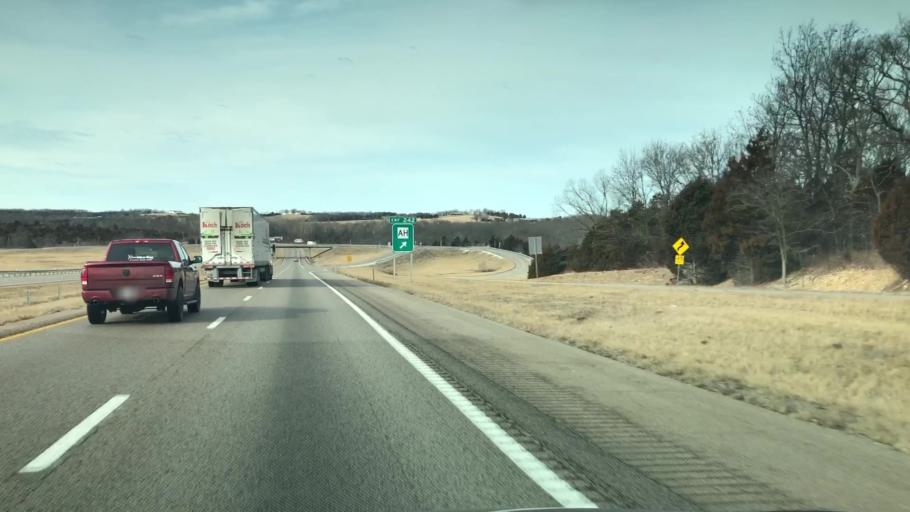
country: US
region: Missouri
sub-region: Franklin County
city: Saint Clair
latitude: 38.3850
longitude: -90.9559
